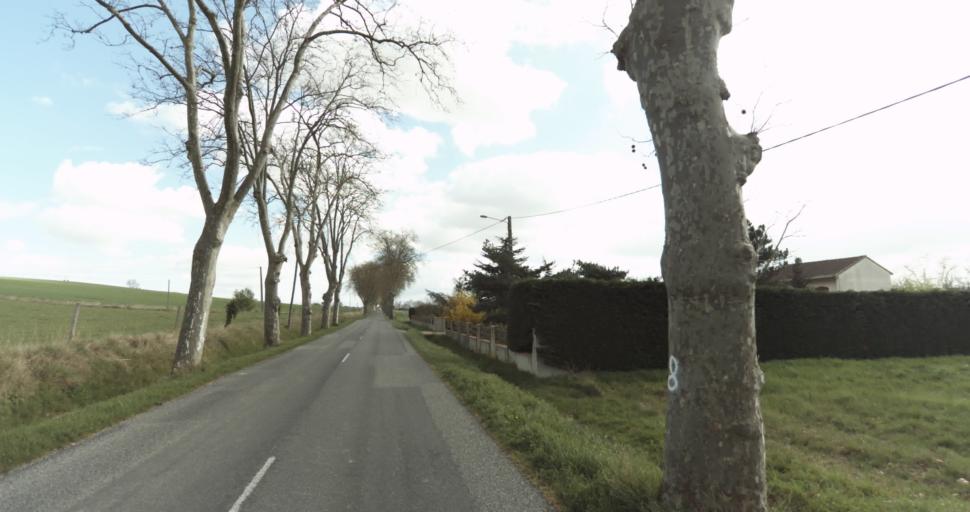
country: FR
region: Midi-Pyrenees
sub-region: Departement de la Haute-Garonne
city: Auterive
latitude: 43.3711
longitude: 1.4694
